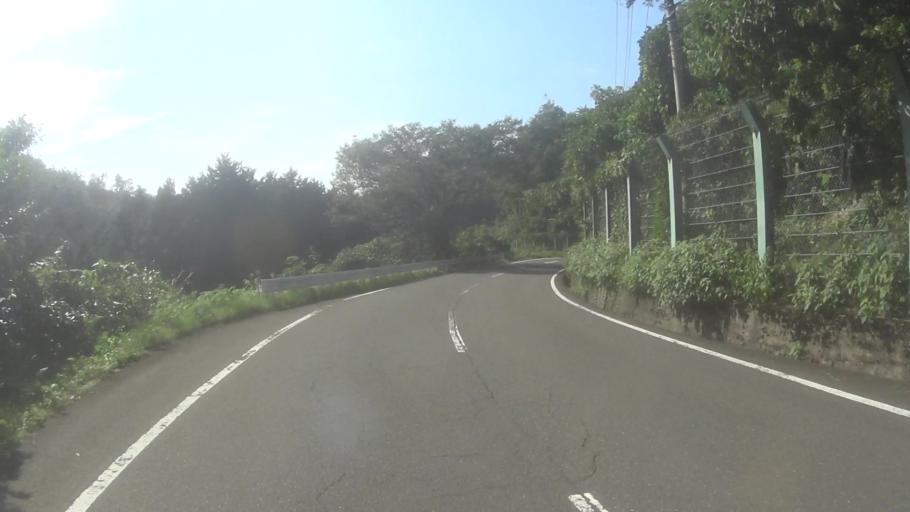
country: JP
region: Kyoto
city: Miyazu
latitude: 35.6896
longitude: 135.1201
